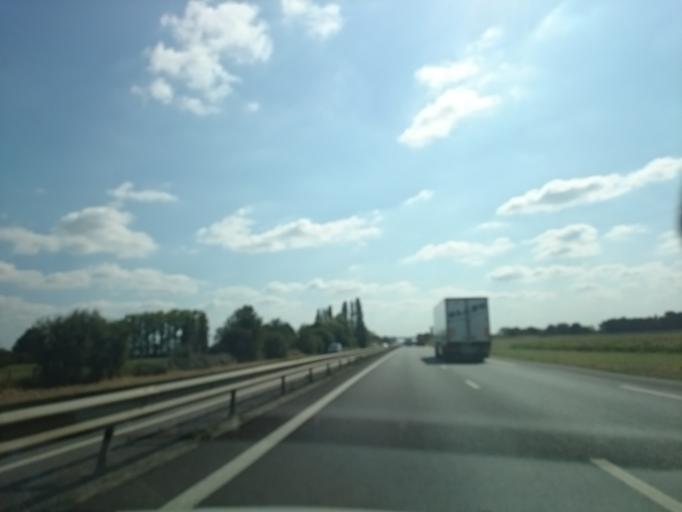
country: FR
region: Brittany
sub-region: Departement d'Ille-et-Vilaine
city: Rennes
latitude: 48.0743
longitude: -1.6757
